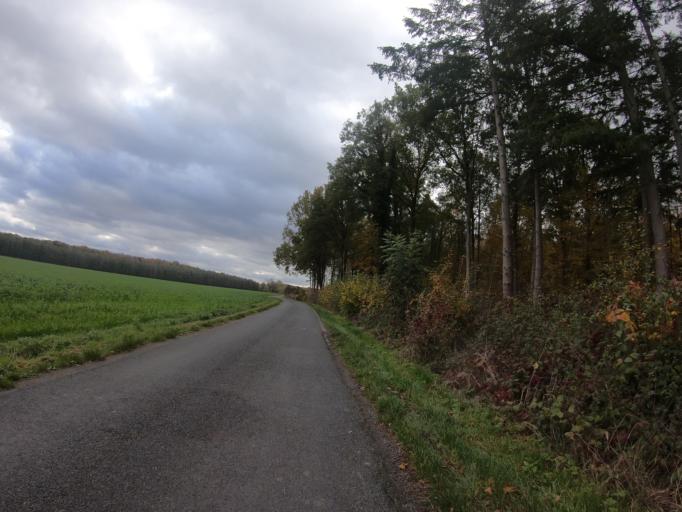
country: DE
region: Lower Saxony
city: Ribbesbuttel
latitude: 52.4099
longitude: 10.4778
